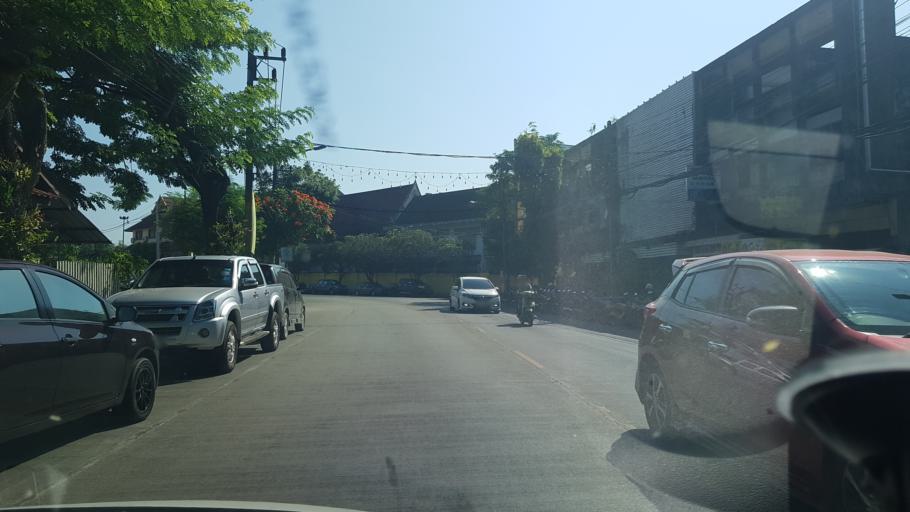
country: TH
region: Chiang Rai
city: Chiang Rai
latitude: 19.9122
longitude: 99.8294
